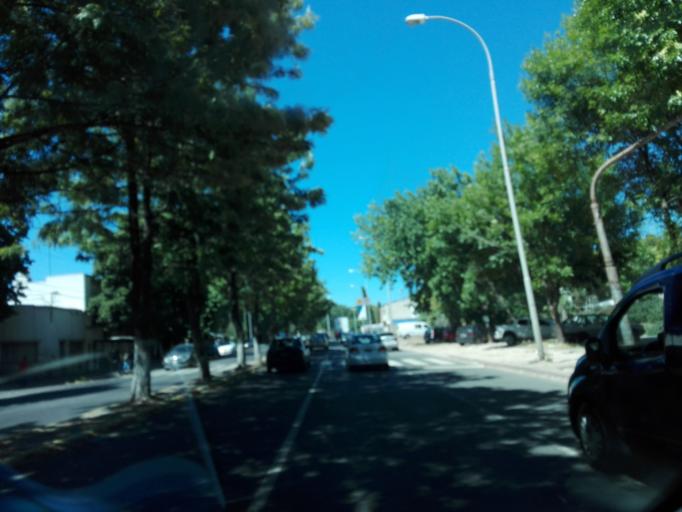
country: AR
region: Buenos Aires
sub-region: Partido de La Plata
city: La Plata
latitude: -34.9061
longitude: -57.9259
